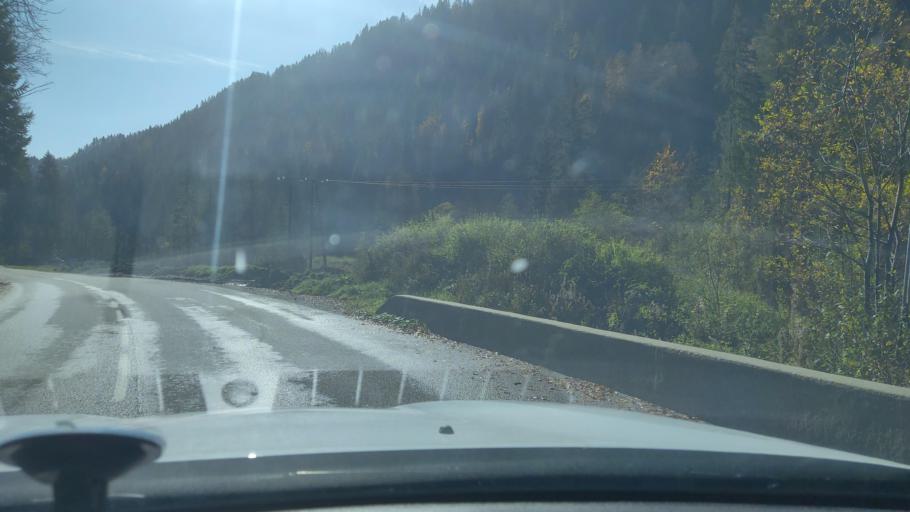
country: FR
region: Rhone-Alpes
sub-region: Departement de la Haute-Savoie
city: Praz-sur-Arly
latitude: 45.8539
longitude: 6.5001
